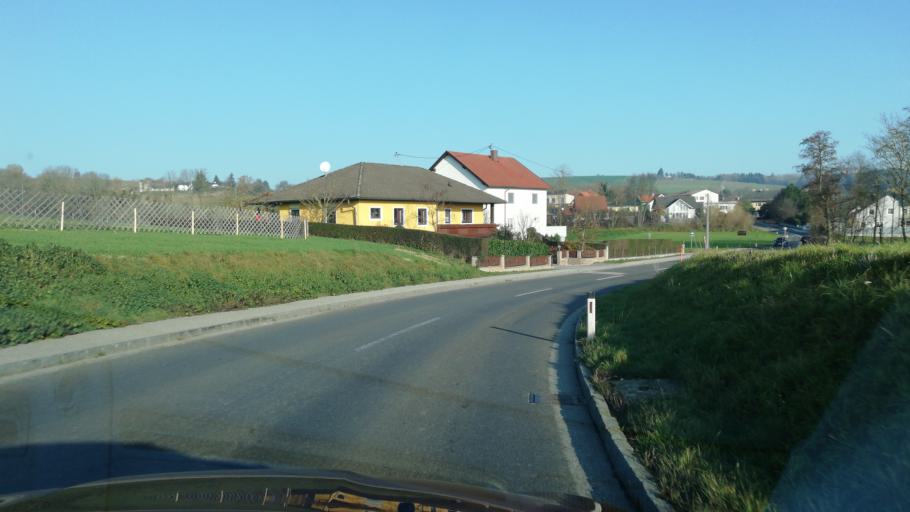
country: AT
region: Upper Austria
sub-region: Wels-Land
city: Buchkirchen
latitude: 48.2330
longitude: 14.0264
